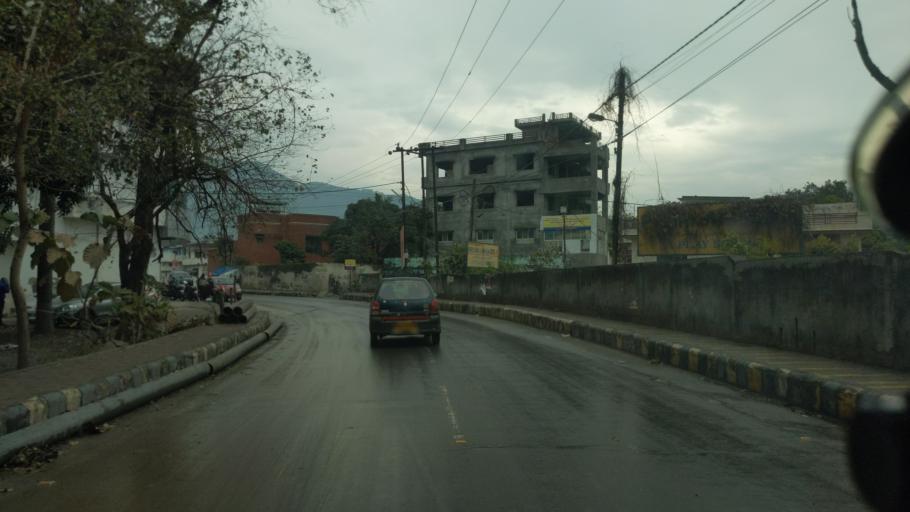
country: IN
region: Uttarakhand
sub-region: Naini Tal
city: Haldwani
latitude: 29.2459
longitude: 79.5352
